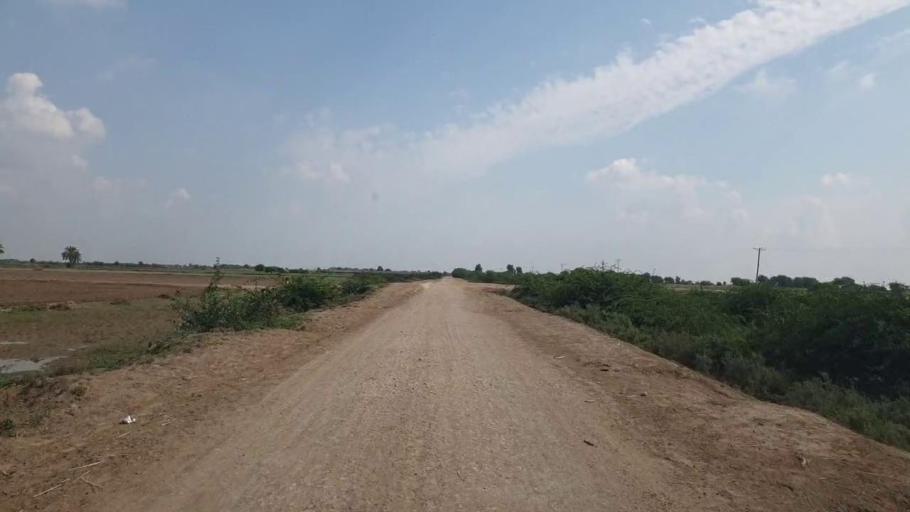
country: PK
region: Sindh
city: Badin
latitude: 24.4774
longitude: 68.6269
